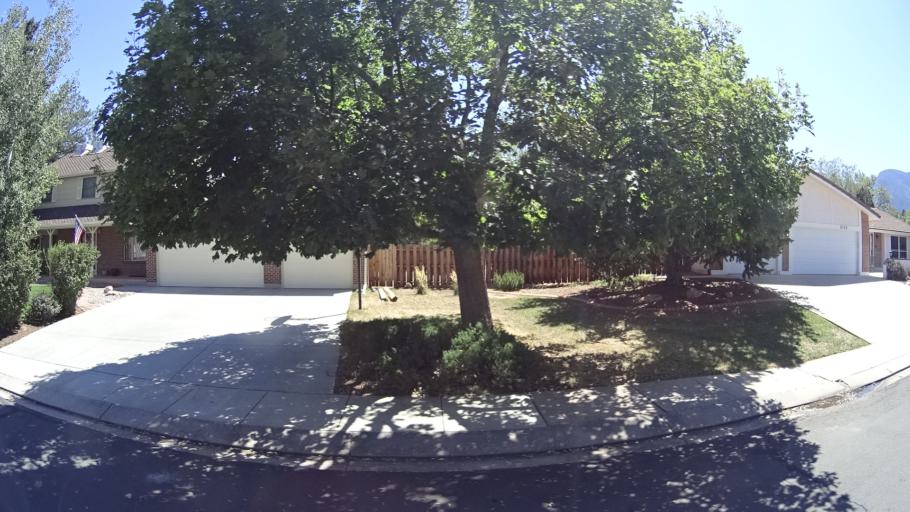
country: US
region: Colorado
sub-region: El Paso County
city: Colorado Springs
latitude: 38.7885
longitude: -104.8309
